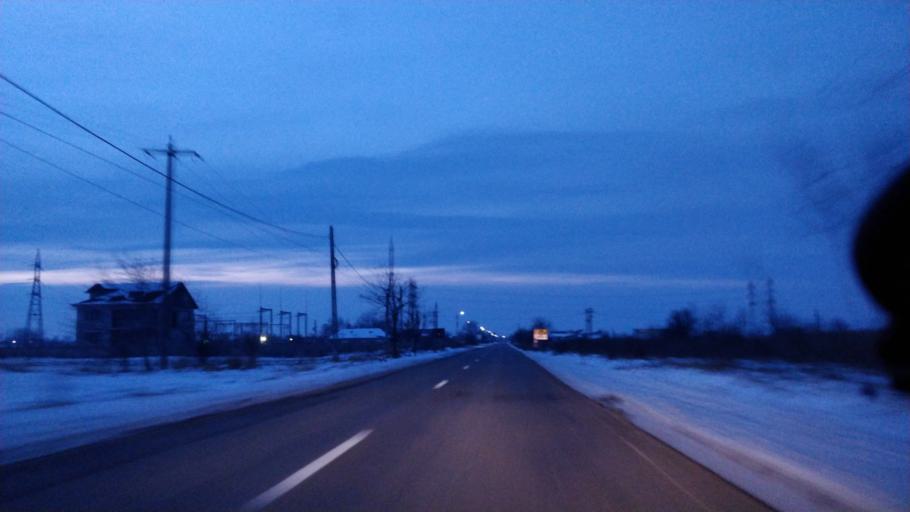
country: RO
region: Vrancea
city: Vulturu de Sus
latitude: 45.6089
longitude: 27.4437
